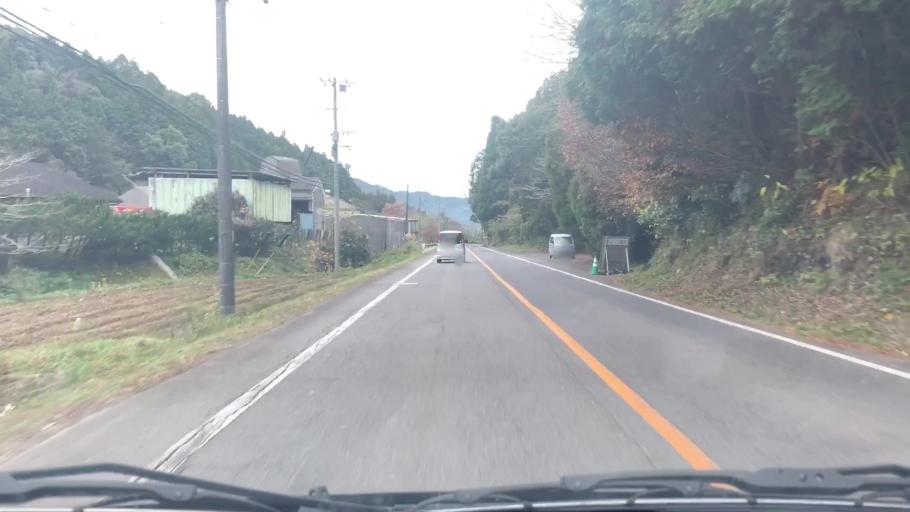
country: JP
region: Saga Prefecture
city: Takeocho-takeo
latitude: 33.1847
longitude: 129.9690
